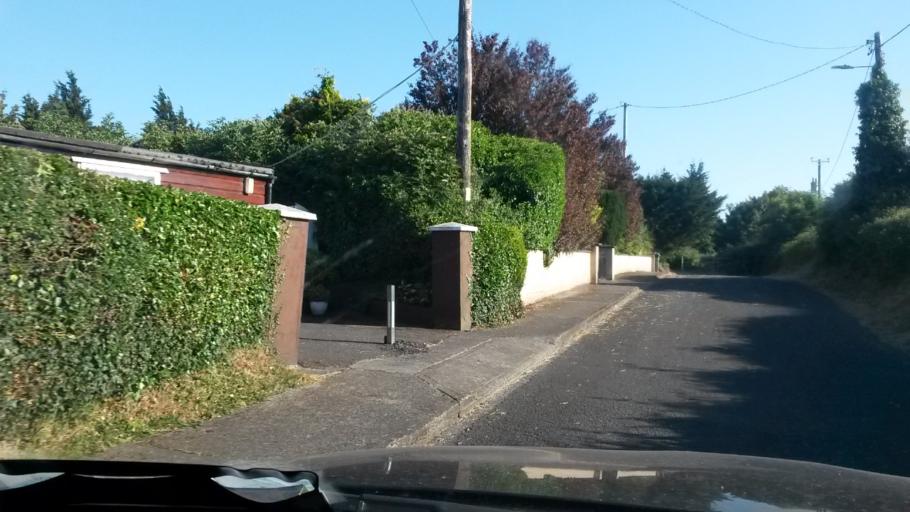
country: IE
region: Leinster
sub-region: Dublin City
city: Finglas
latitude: 53.4255
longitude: -6.3156
